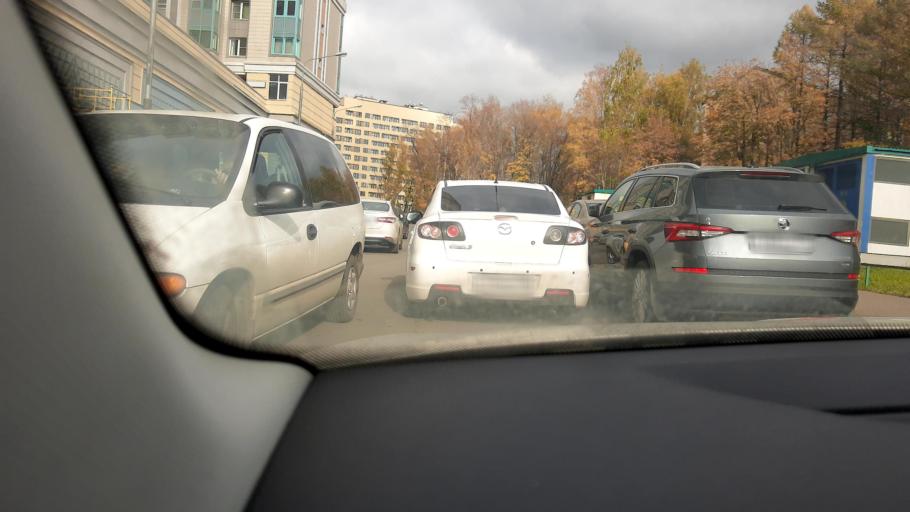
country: RU
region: Moscow
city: Zagor'ye
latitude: 55.5788
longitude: 37.6717
